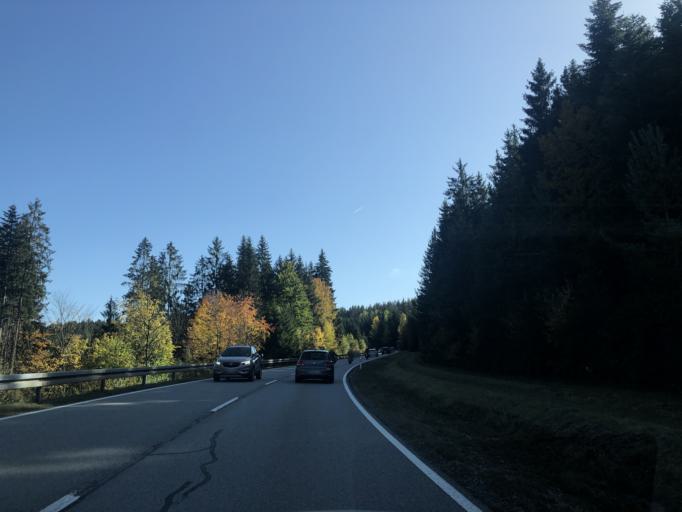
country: DE
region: Bavaria
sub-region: Lower Bavaria
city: Langdorf
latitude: 49.0210
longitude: 13.1375
